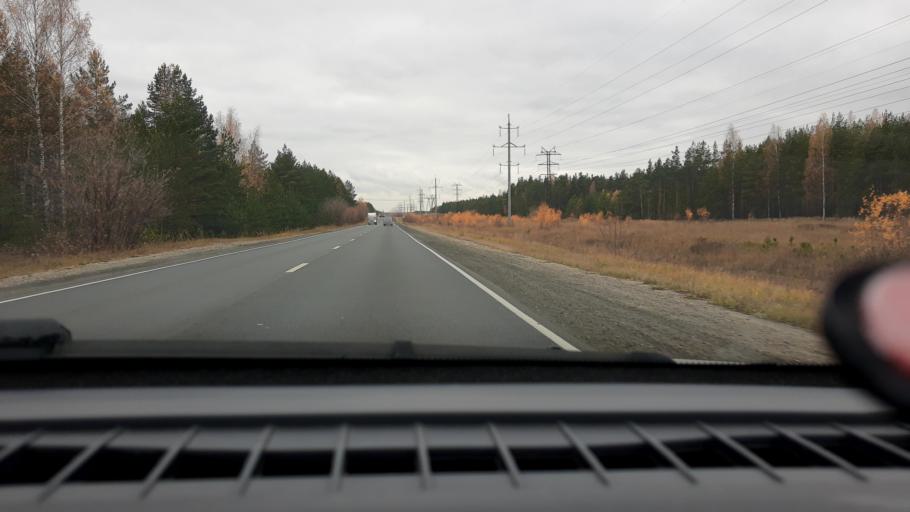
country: RU
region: Nizjnij Novgorod
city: Lukino
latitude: 56.3967
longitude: 43.6481
